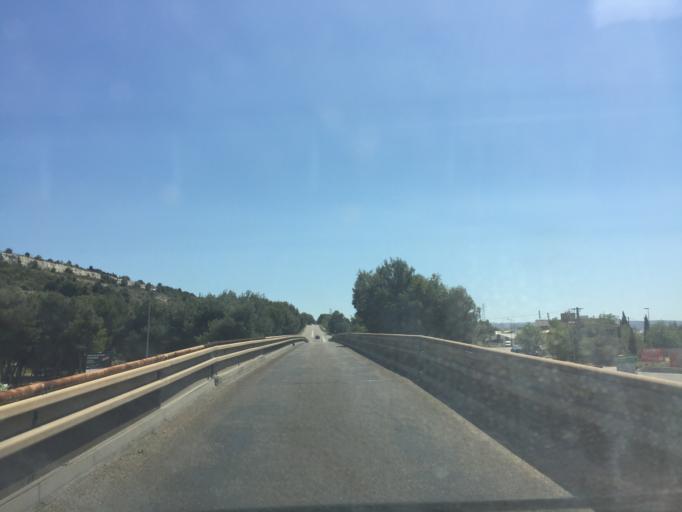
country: FR
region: Provence-Alpes-Cote d'Azur
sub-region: Departement des Bouches-du-Rhone
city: Vitrolles
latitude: 43.4600
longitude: 5.2329
